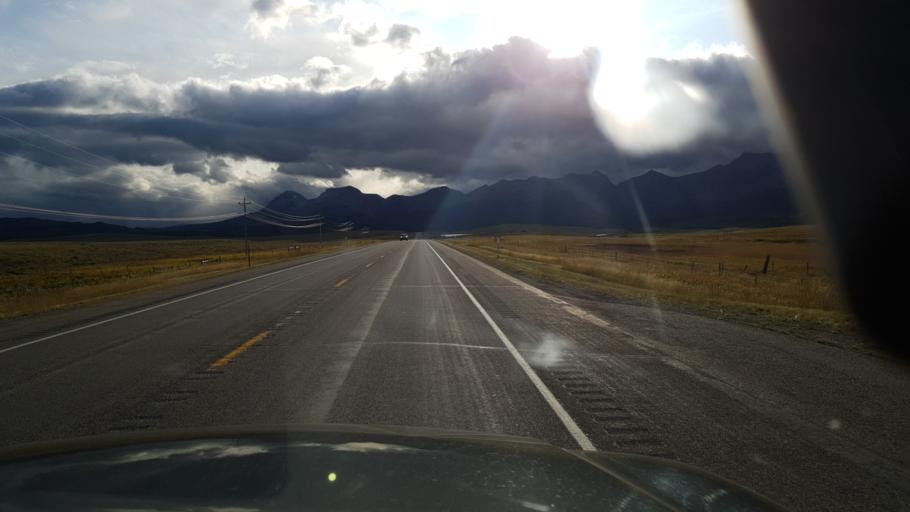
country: US
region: Montana
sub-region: Glacier County
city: South Browning
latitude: 48.4609
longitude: -113.1715
